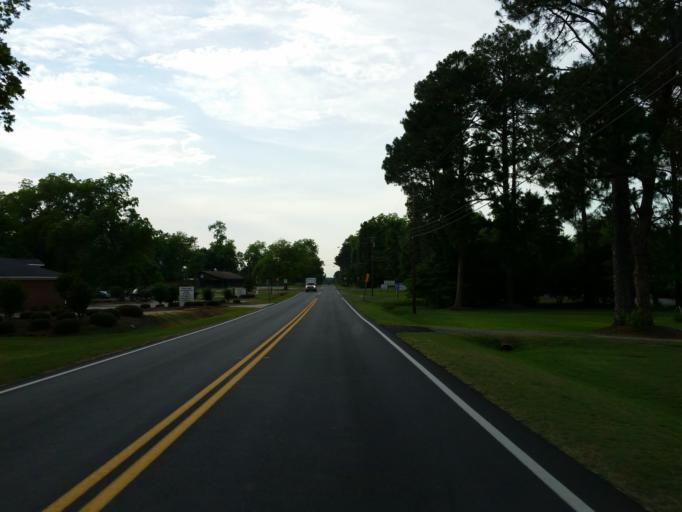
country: US
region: Georgia
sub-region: Dooly County
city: Unadilla
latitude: 32.2677
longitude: -83.7360
